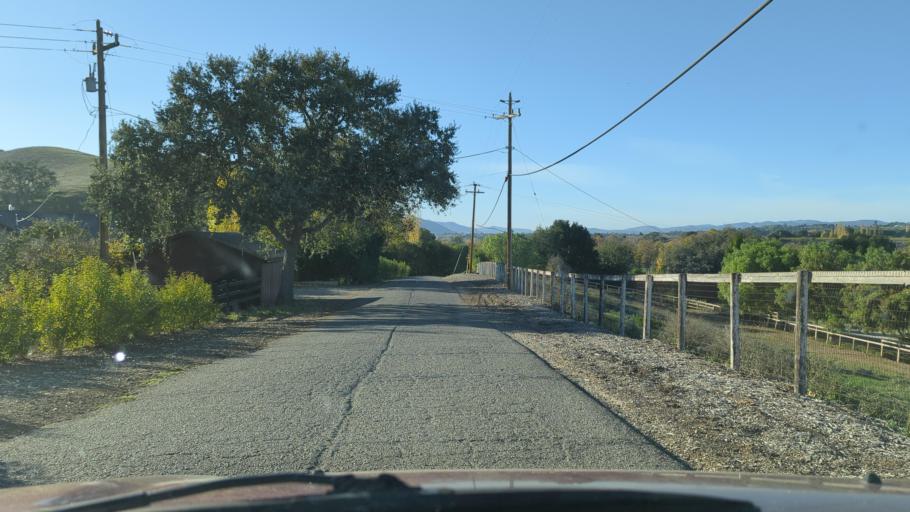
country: US
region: California
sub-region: Santa Barbara County
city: Solvang
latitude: 34.5798
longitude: -120.1007
